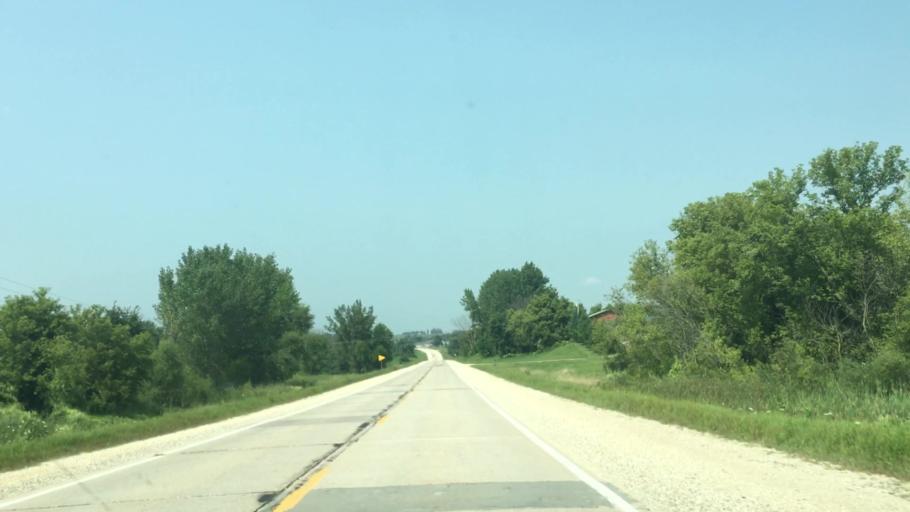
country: US
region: Iowa
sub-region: Fayette County
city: West Union
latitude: 43.1083
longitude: -91.8691
